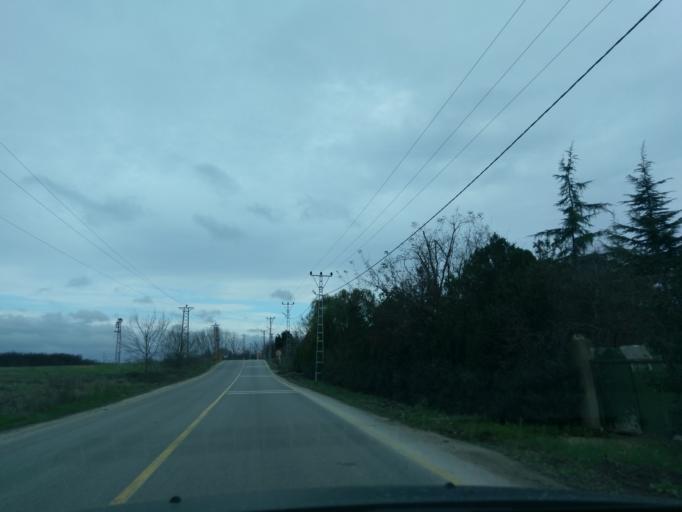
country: TR
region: Istanbul
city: Catalca
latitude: 41.2033
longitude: 28.3865
